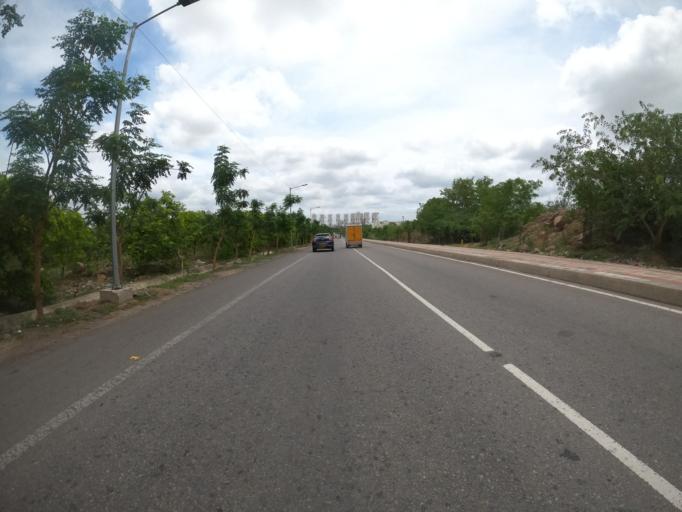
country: IN
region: Telangana
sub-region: Hyderabad
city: Hyderabad
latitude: 17.3802
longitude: 78.3504
